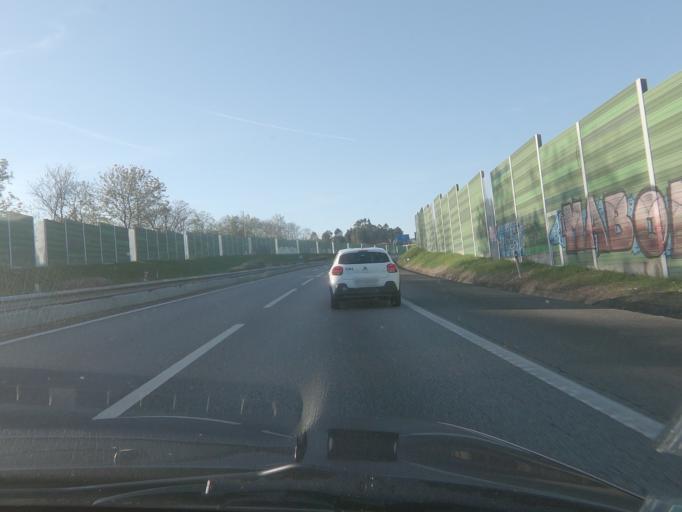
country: PT
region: Porto
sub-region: Santo Tirso
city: Santo Tirso
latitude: 41.3694
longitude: -8.5028
